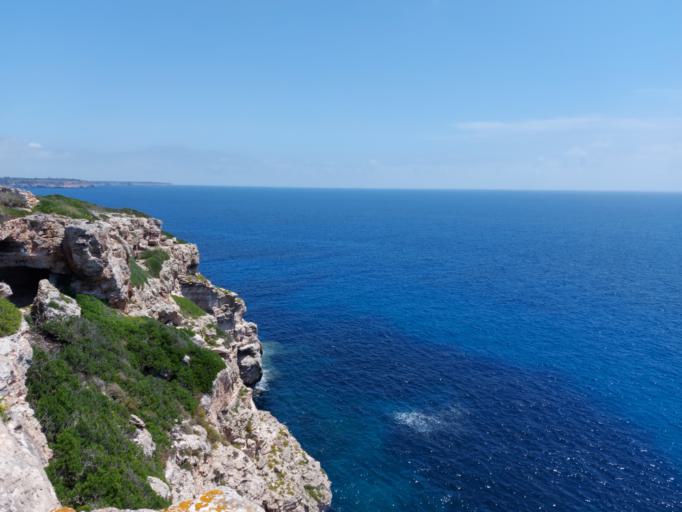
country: ES
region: Balearic Islands
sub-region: Illes Balears
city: Ses Salines
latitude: 39.2943
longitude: 3.0999
